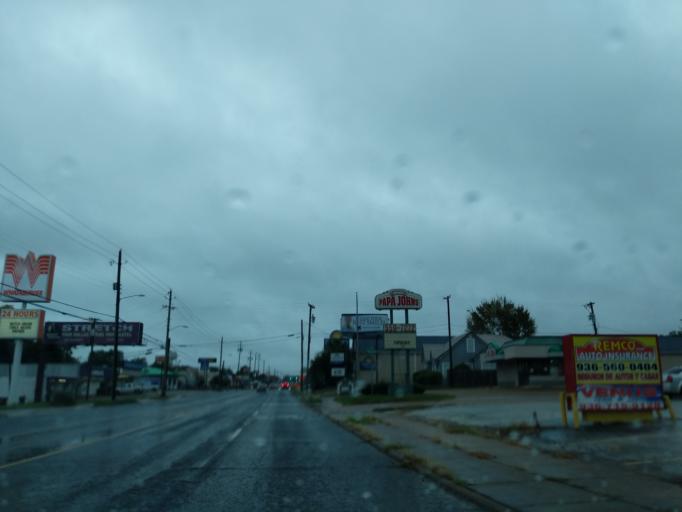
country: US
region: Texas
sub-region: Nacogdoches County
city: Nacogdoches
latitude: 31.6272
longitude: -94.6523
